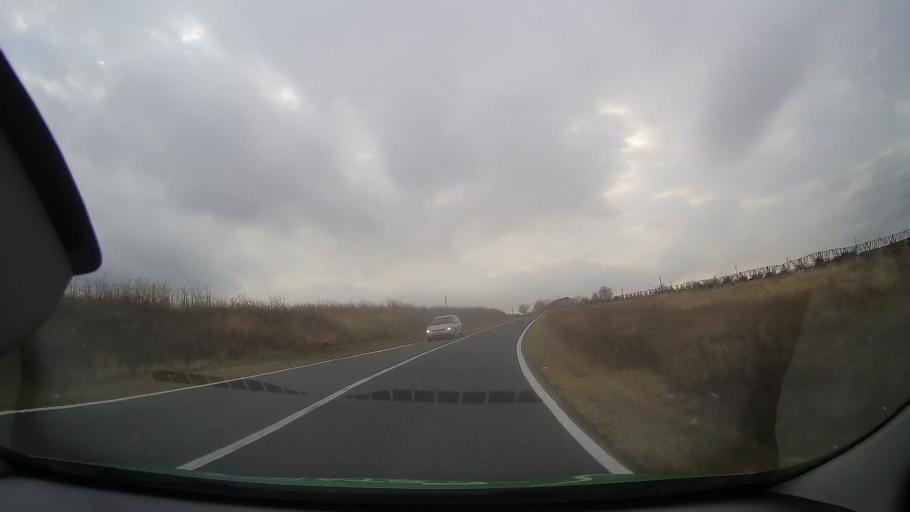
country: RO
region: Constanta
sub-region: Comuna Deleni
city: Deleni
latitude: 44.0928
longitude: 28.0168
